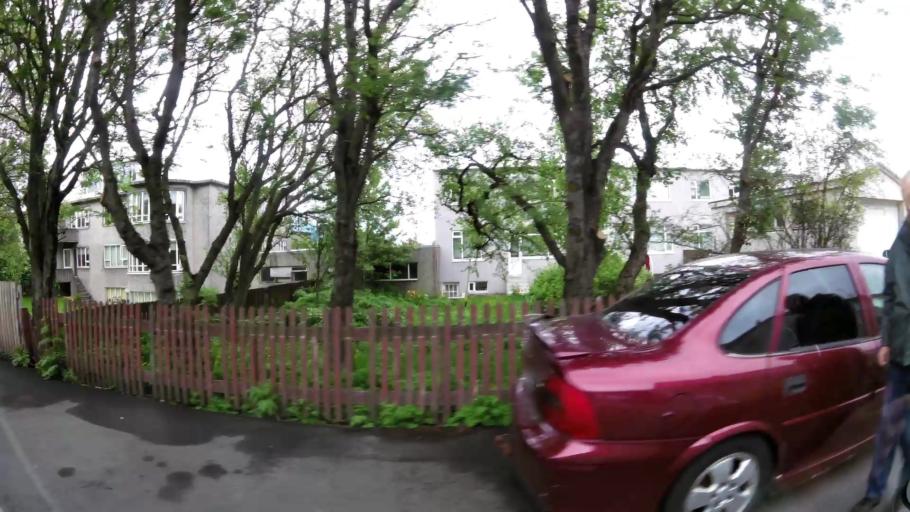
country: IS
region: Capital Region
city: Reykjavik
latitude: 64.1357
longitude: -21.9184
